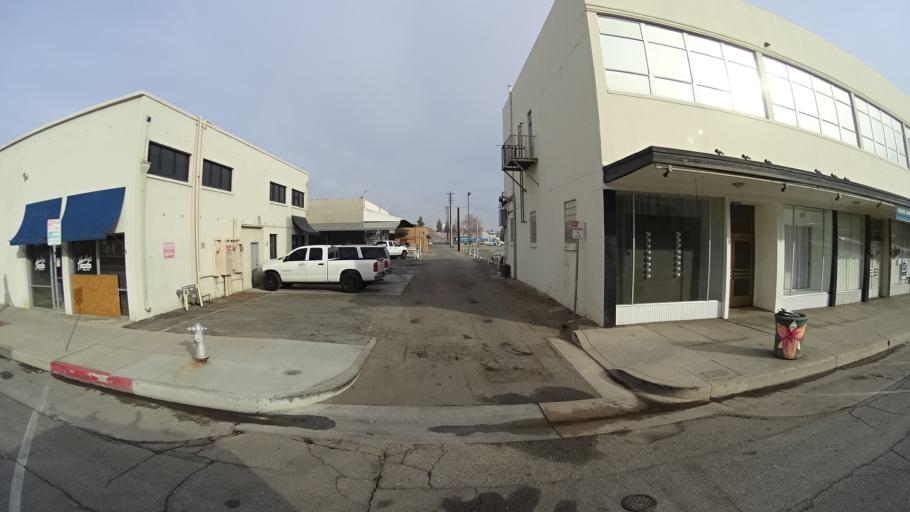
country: US
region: California
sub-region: Kern County
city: Bakersfield
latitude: 35.3772
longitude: -119.0206
